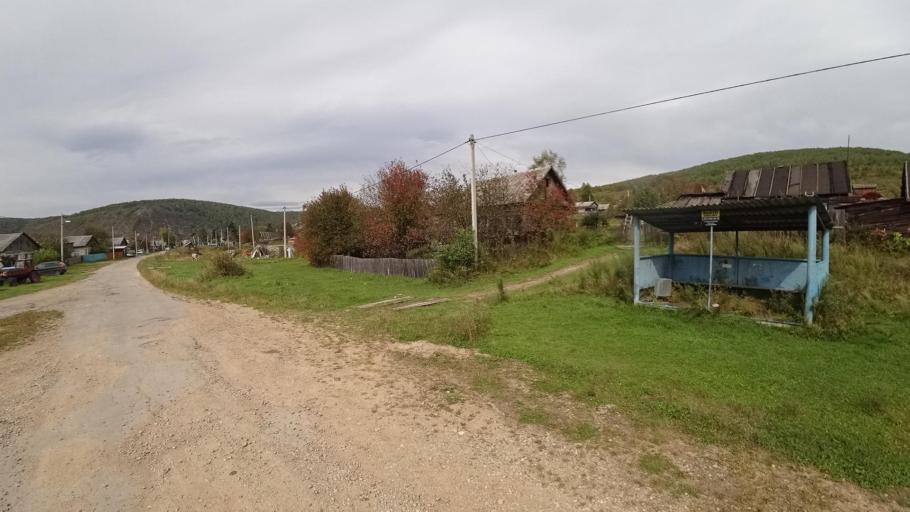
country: RU
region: Jewish Autonomous Oblast
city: Khingansk
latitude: 49.1217
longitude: 131.2060
